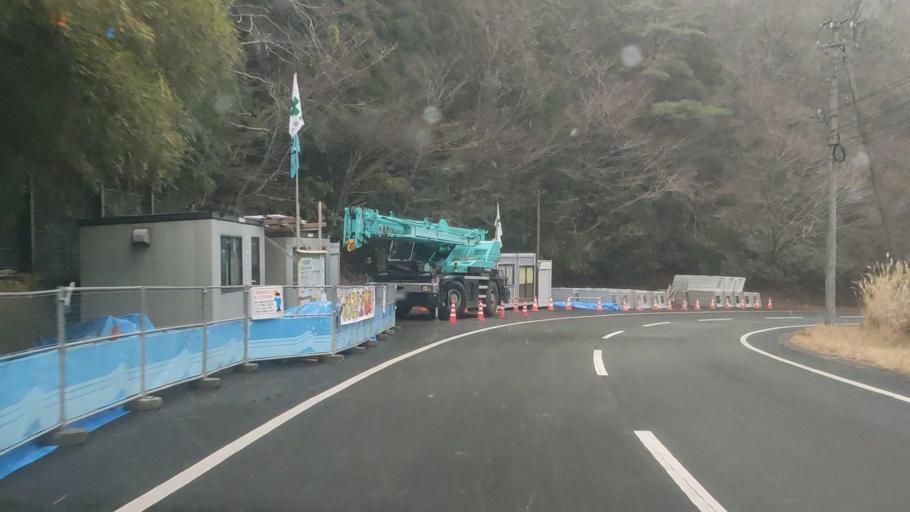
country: JP
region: Kumamoto
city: Matsubase
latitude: 32.5537
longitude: 130.9338
